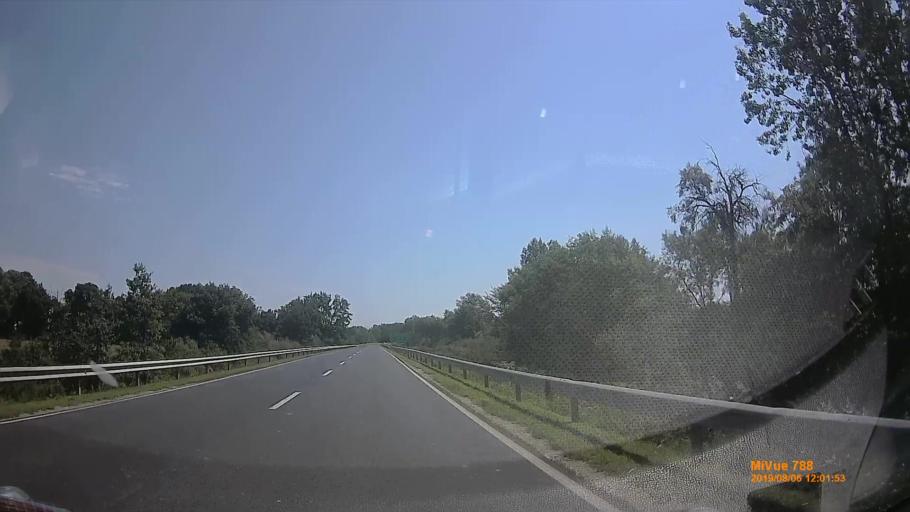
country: HU
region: Vas
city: Vasvar
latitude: 47.0582
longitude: 16.7749
